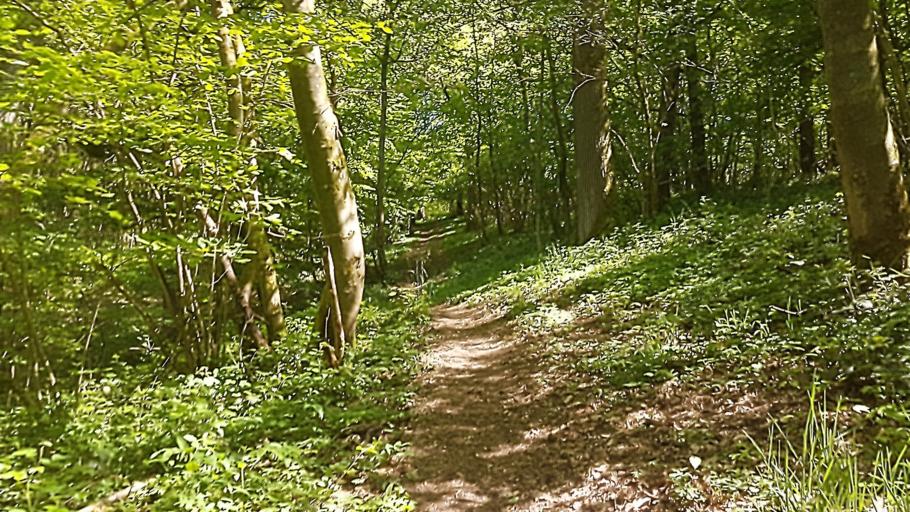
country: BE
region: Wallonia
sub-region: Province de Namur
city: Couvin
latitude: 50.0575
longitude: 4.5759
